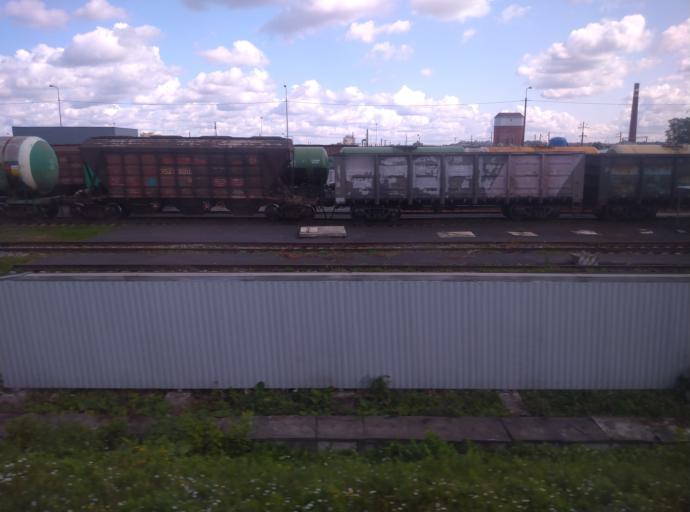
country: RU
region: St.-Petersburg
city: Obukhovo
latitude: 59.8722
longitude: 30.4171
